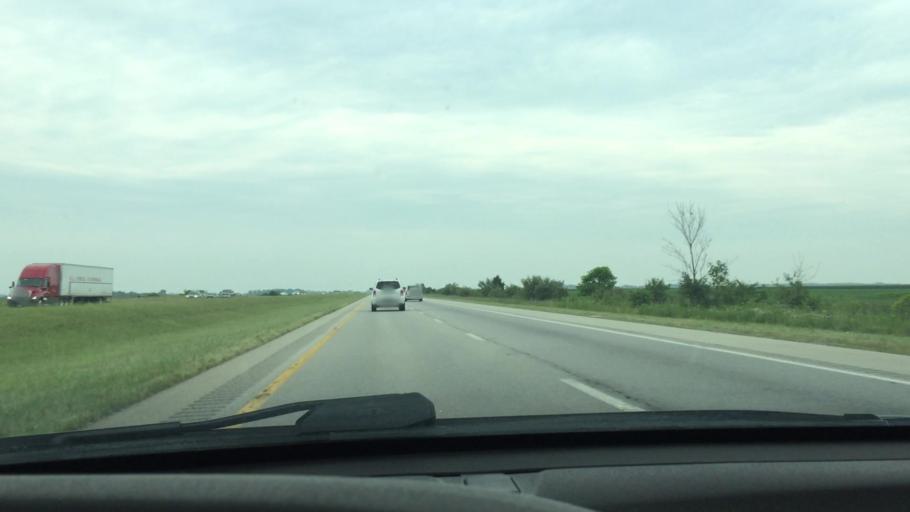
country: US
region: Ohio
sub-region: Clinton County
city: Wilmington
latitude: 39.5377
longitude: -83.7781
